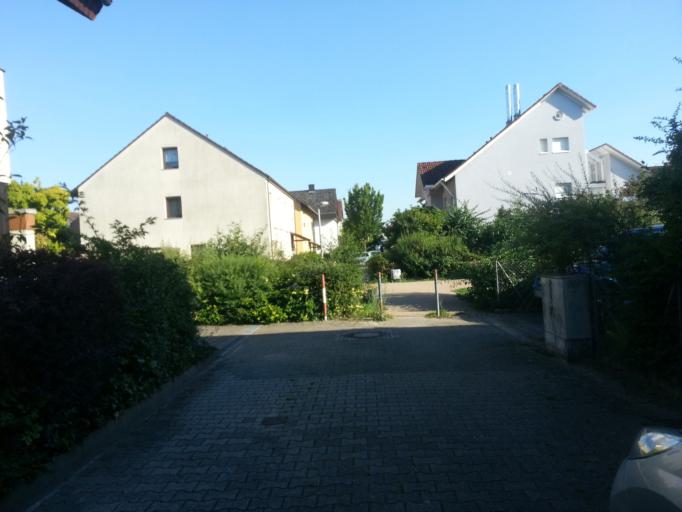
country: DE
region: Baden-Wuerttemberg
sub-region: Karlsruhe Region
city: Ilvesheim
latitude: 49.4680
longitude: 8.5528
